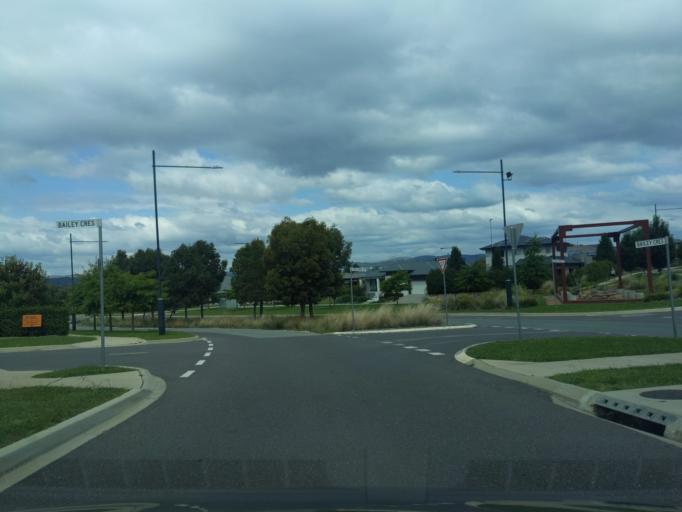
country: AU
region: New South Wales
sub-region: Queanbeyan
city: Queanbeyan
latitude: -35.4177
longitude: 149.2294
